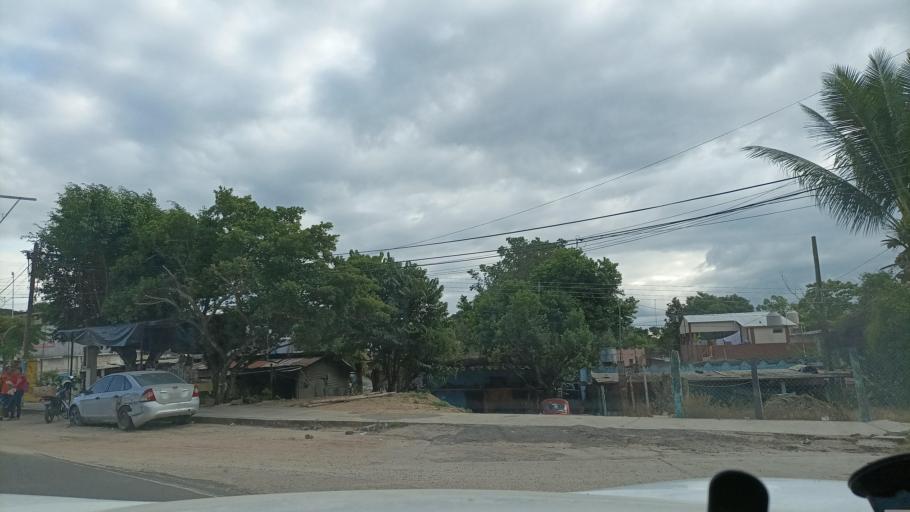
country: MX
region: Veracruz
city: Oluta
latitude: 17.9260
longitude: -94.8897
